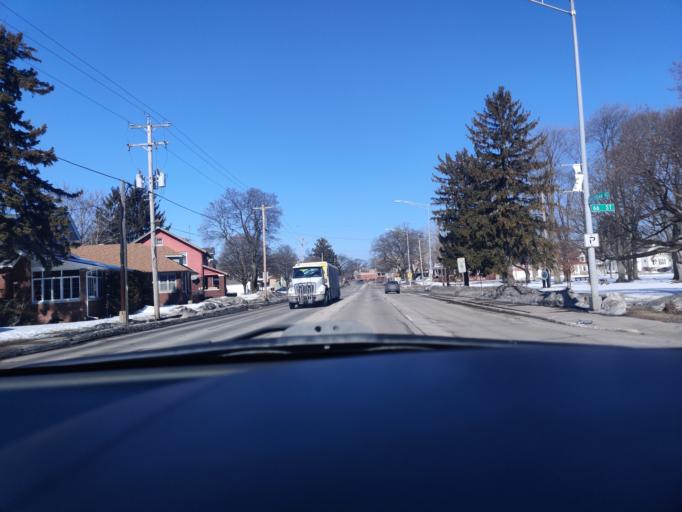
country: US
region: Wisconsin
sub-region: Kenosha County
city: Kenosha
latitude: 42.5744
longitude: -87.8222
